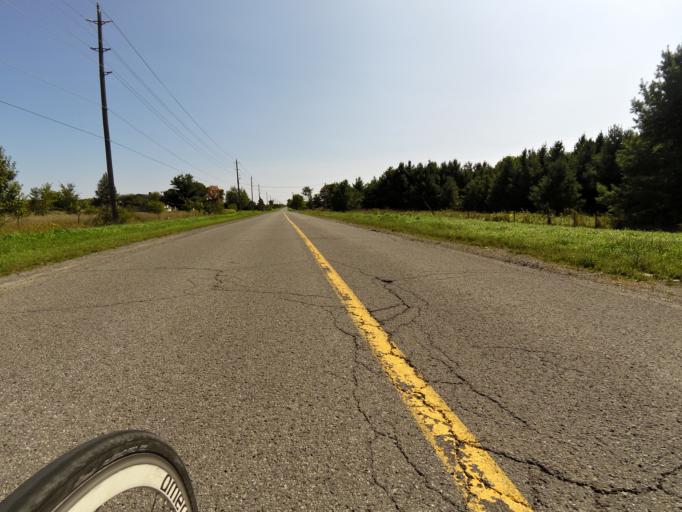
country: CA
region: Ontario
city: Arnprior
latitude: 45.4843
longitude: -76.1279
